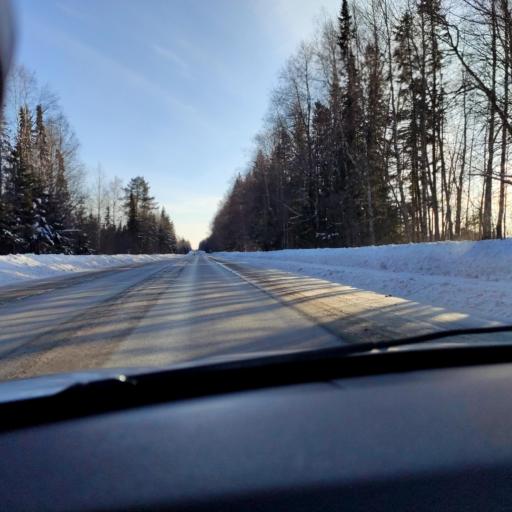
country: RU
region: Perm
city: Dobryanka
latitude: 58.4155
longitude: 56.5202
